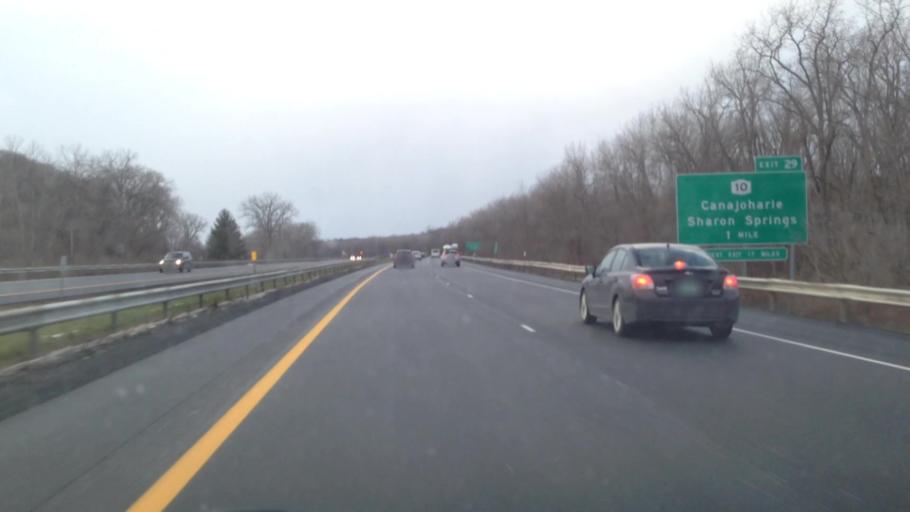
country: US
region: New York
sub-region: Montgomery County
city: Canajoharie
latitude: 42.8992
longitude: -74.5424
